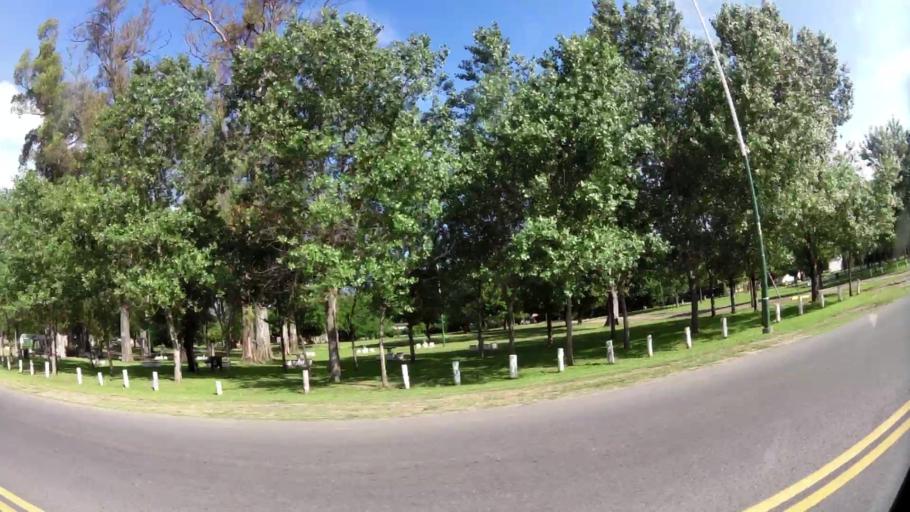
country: AR
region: Buenos Aires
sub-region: Partido de Merlo
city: Merlo
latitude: -34.6533
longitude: -58.7481
